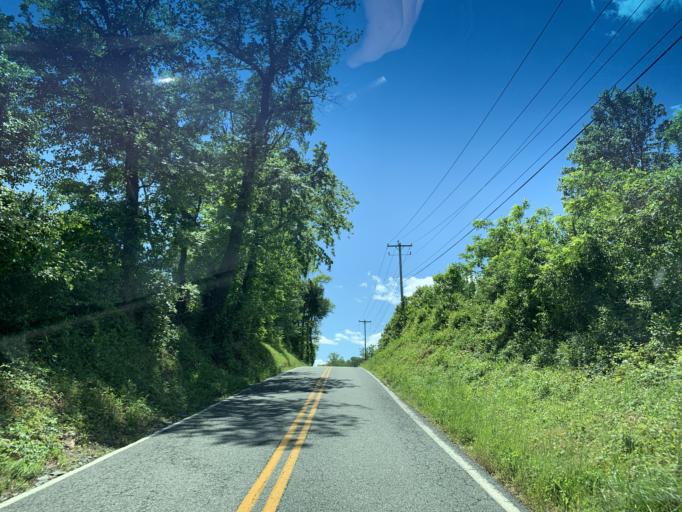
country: US
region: Maryland
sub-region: Cecil County
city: Charlestown
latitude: 39.5174
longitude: -75.9459
